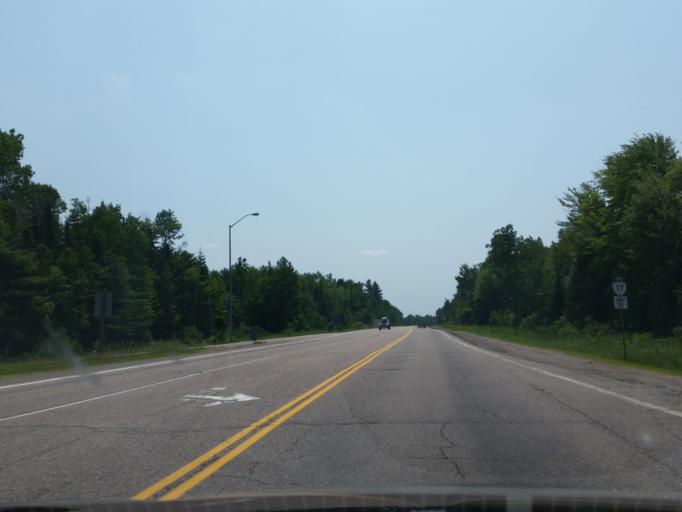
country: CA
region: Ontario
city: Petawawa
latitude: 45.8801
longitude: -77.3033
